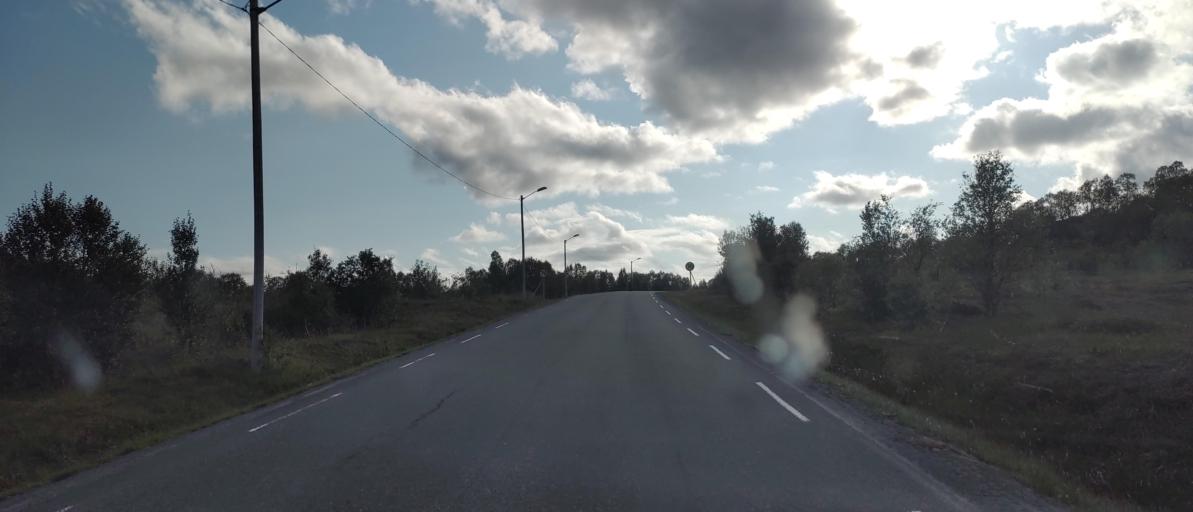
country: NO
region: Nordland
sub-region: Sortland
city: Sortland
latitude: 68.7213
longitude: 15.4652
